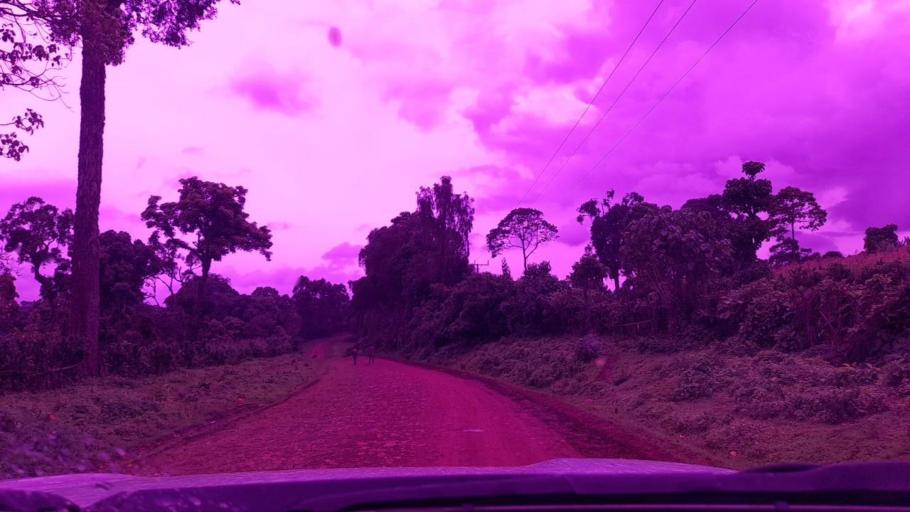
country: ET
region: Southern Nations, Nationalities, and People's Region
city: Tippi
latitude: 7.5809
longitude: 35.6277
